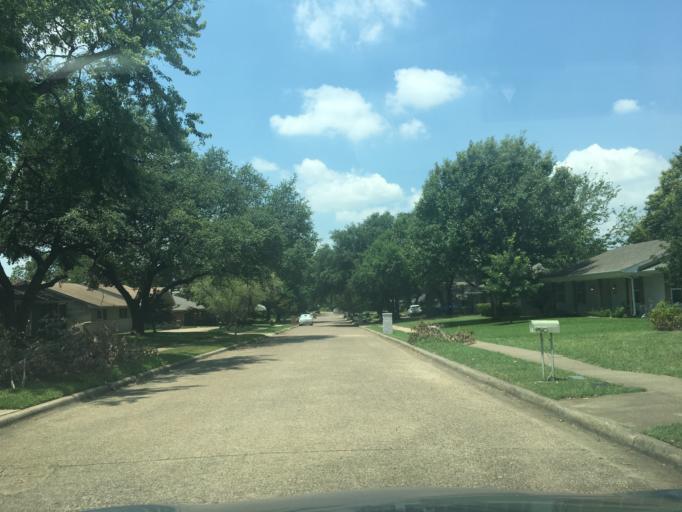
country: US
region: Texas
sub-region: Dallas County
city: Addison
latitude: 32.9206
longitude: -96.8394
